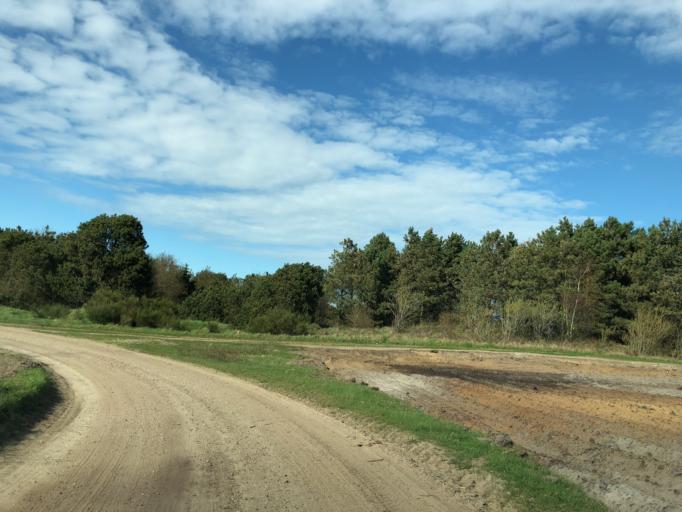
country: DK
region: Central Jutland
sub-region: Holstebro Kommune
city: Ulfborg
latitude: 56.2427
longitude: 8.3451
